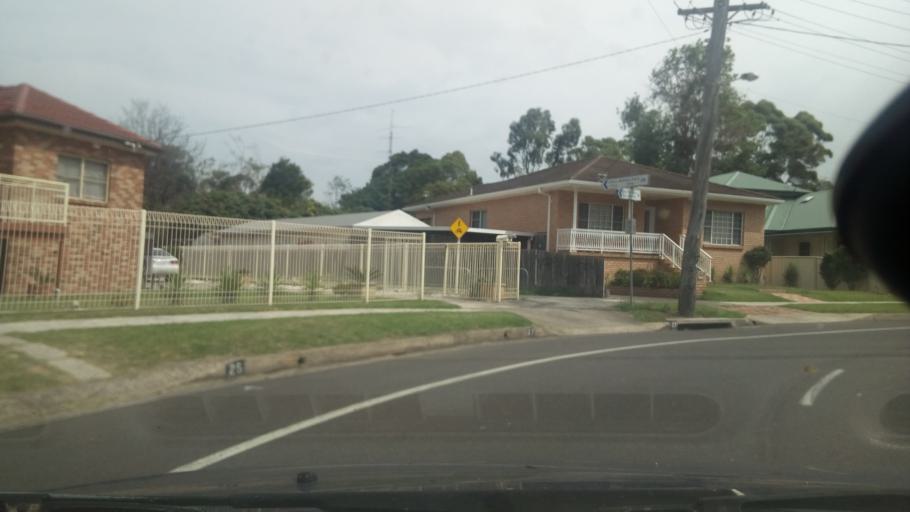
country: AU
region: New South Wales
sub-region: Wollongong
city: Gwynneville
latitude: -34.4147
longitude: 150.8902
